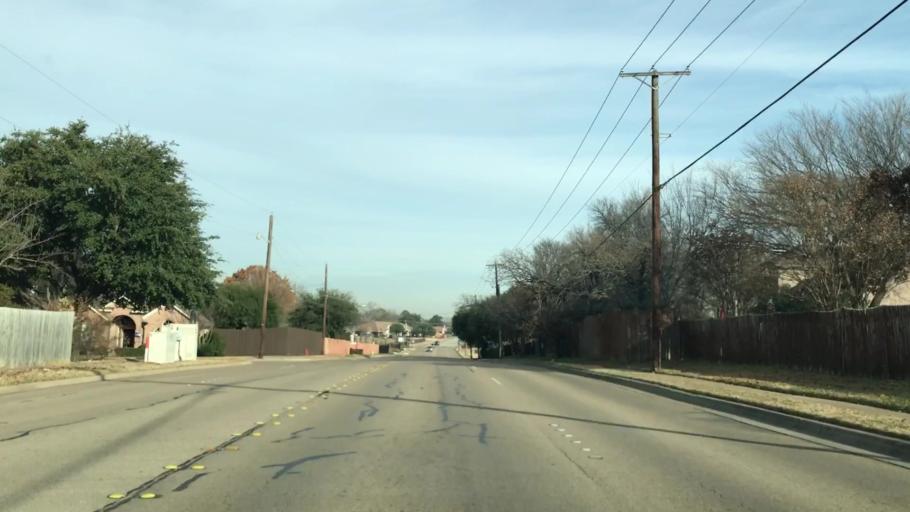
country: US
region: Texas
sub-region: Tarrant County
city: Watauga
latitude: 32.8789
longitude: -97.2120
